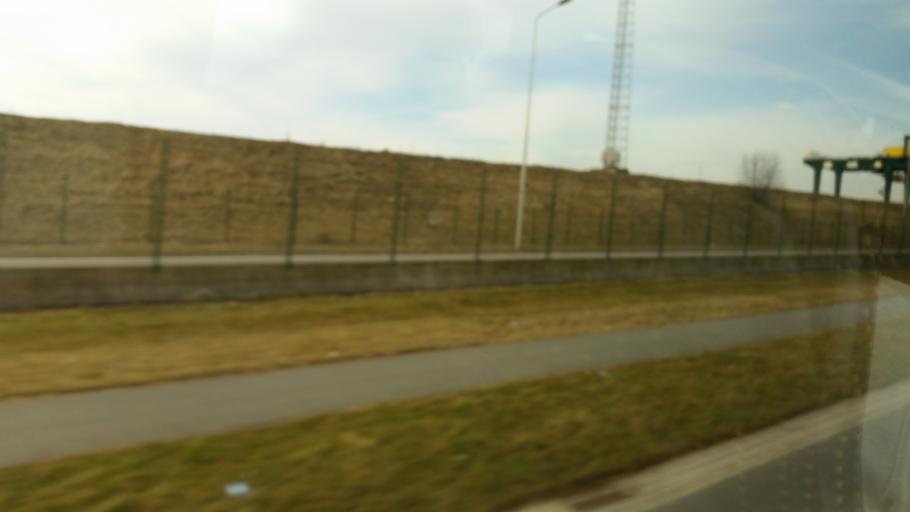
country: BE
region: Flanders
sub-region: Provincie Oost-Vlaanderen
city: Beveren
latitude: 51.2862
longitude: 4.2427
